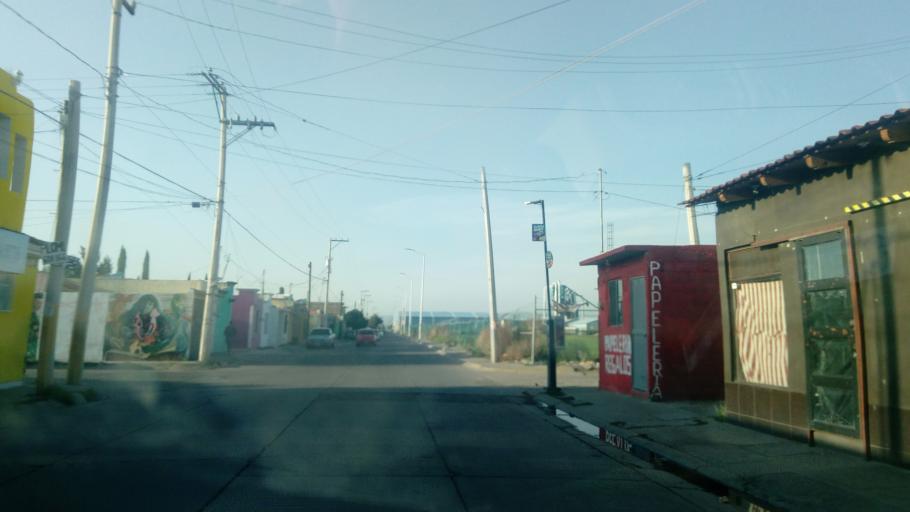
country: MX
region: Durango
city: Victoria de Durango
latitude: 24.0683
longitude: -104.5890
